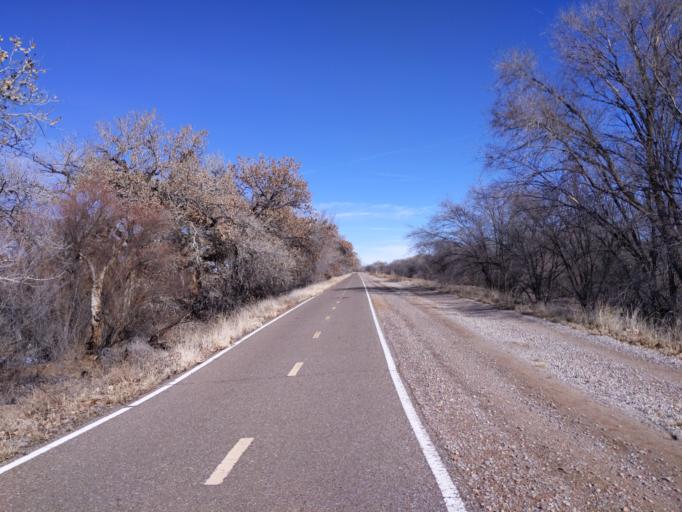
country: US
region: New Mexico
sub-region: Bernalillo County
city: Lee Acres
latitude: 35.1544
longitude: -106.6691
